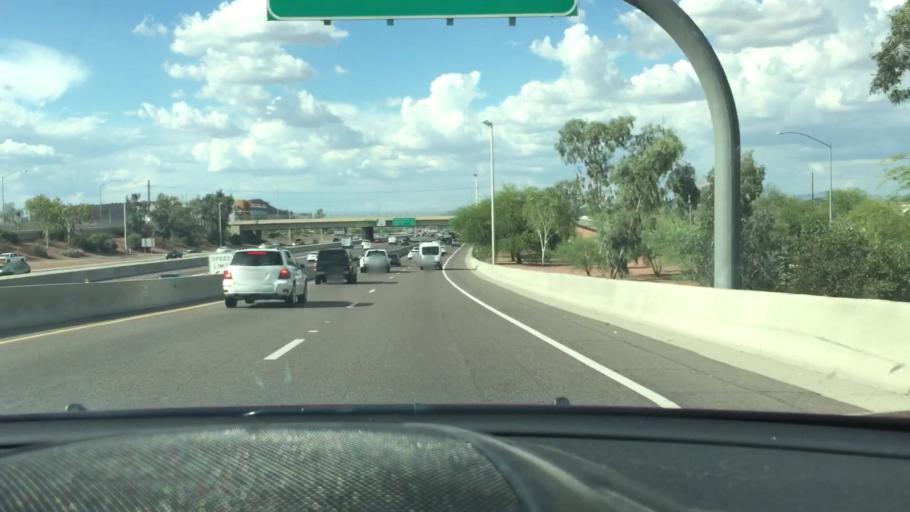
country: US
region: Arizona
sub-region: Maricopa County
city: Glendale
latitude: 33.6734
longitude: -112.1145
